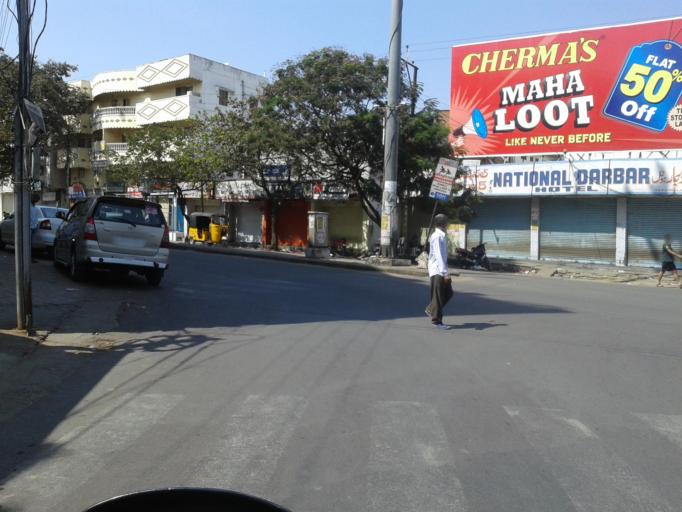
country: IN
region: Telangana
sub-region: Hyderabad
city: Hyderabad
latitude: 17.3937
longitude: 78.4835
